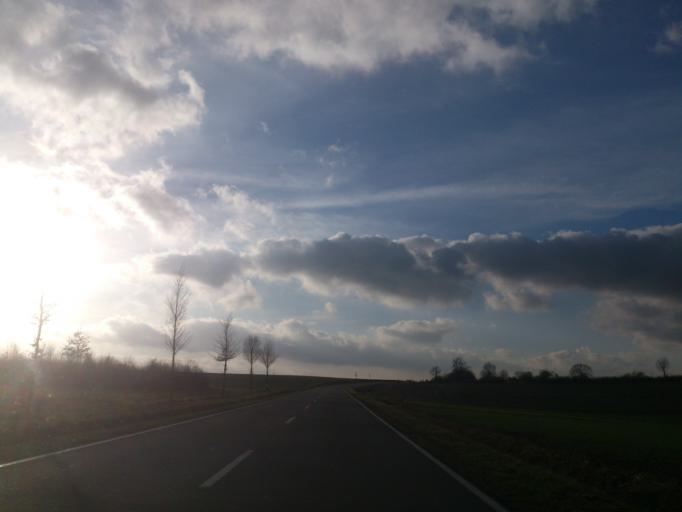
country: DE
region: Lower Saxony
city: Boffzen
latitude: 51.7586
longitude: 9.3285
